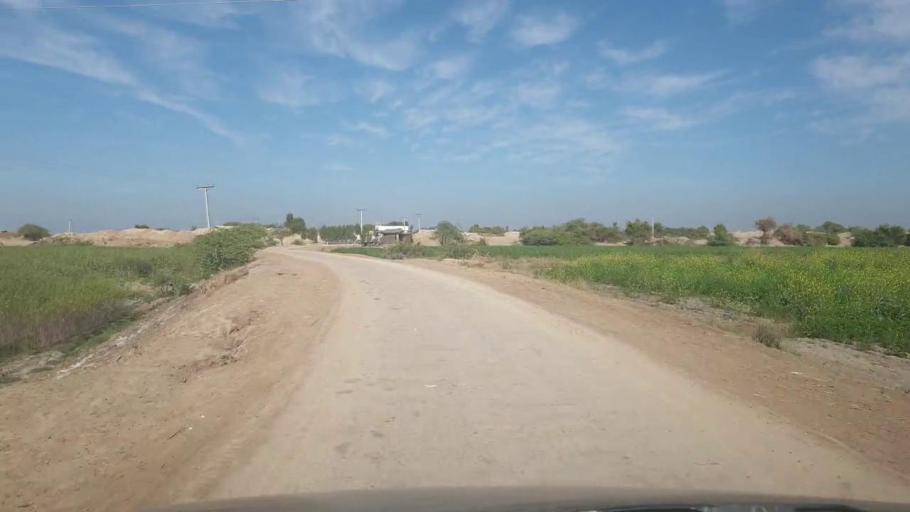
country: PK
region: Sindh
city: Pithoro
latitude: 25.4419
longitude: 69.2113
